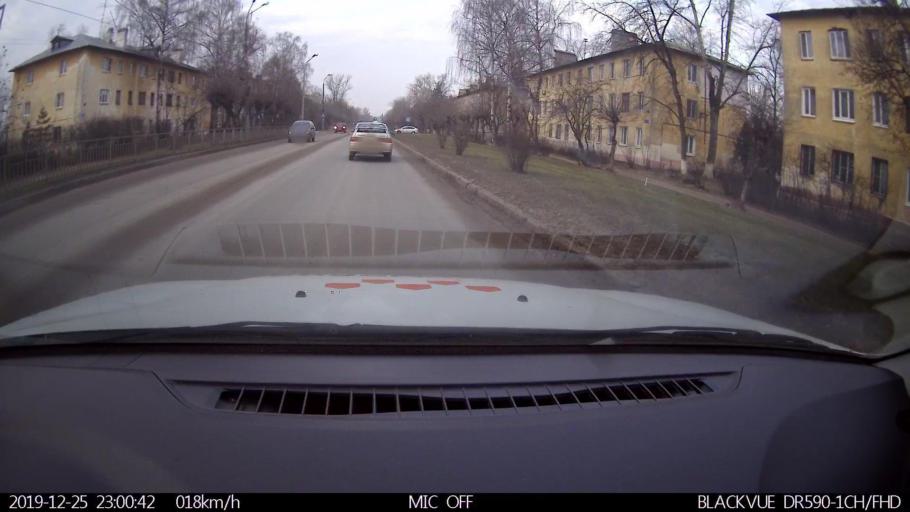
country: RU
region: Nizjnij Novgorod
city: Gorbatovka
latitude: 56.3517
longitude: 43.8351
